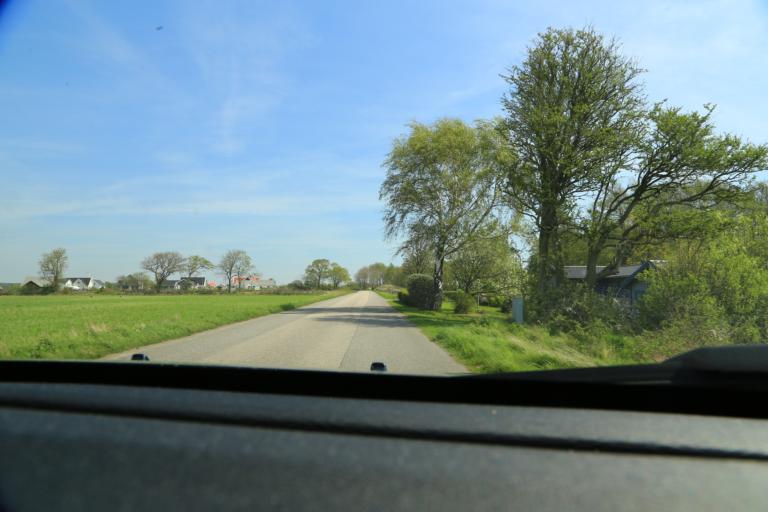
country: SE
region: Halland
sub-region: Varbergs Kommun
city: Varberg
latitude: 57.1421
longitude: 12.2301
